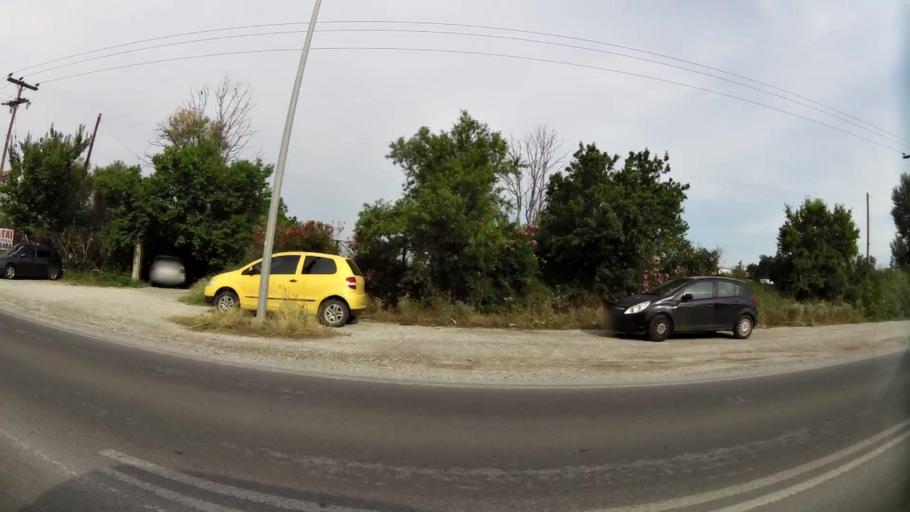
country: GR
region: Central Macedonia
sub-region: Nomos Thessalonikis
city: Thermi
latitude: 40.5557
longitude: 23.0192
